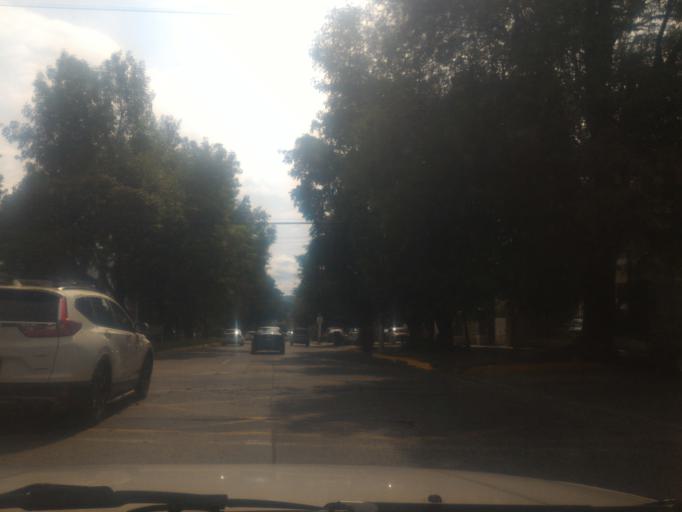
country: MX
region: Jalisco
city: Guadalajara
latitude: 20.6622
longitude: -103.4246
